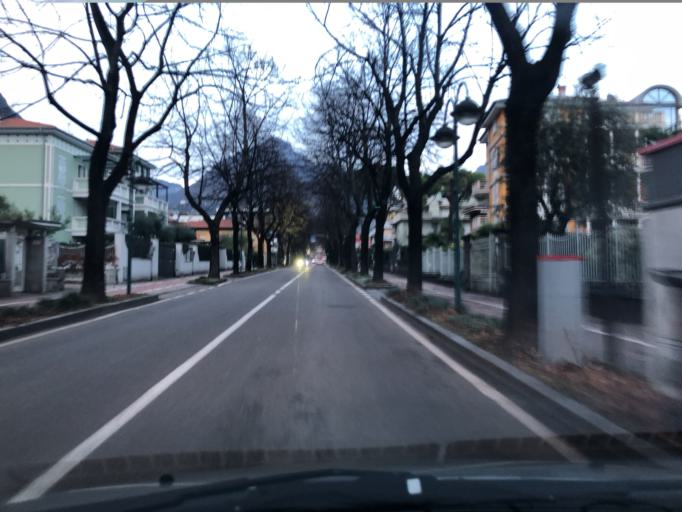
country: IT
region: Trentino-Alto Adige
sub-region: Provincia di Trento
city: Riva del Garda
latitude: 45.8905
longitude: 10.8430
